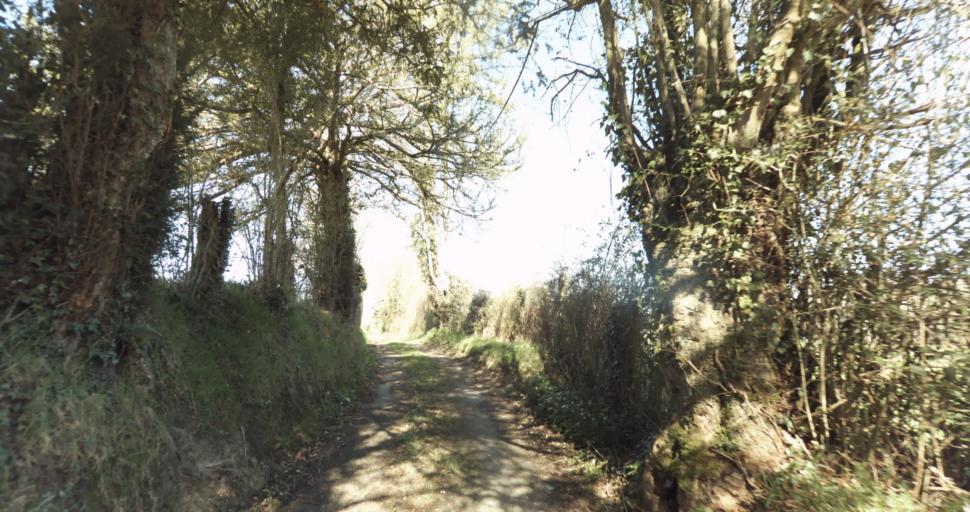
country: FR
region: Lower Normandy
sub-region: Departement du Calvados
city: Livarot
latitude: 48.9869
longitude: 0.0744
